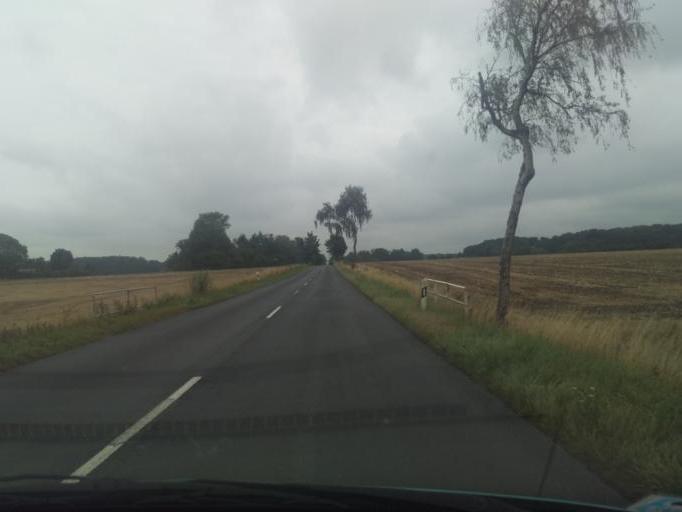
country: DE
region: Lower Saxony
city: Arpke
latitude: 52.3266
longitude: 10.1133
